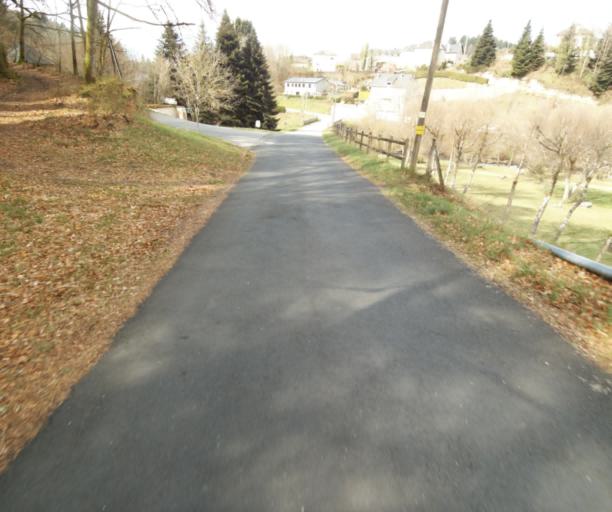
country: FR
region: Limousin
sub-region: Departement de la Correze
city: Correze
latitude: 45.3727
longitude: 1.8815
